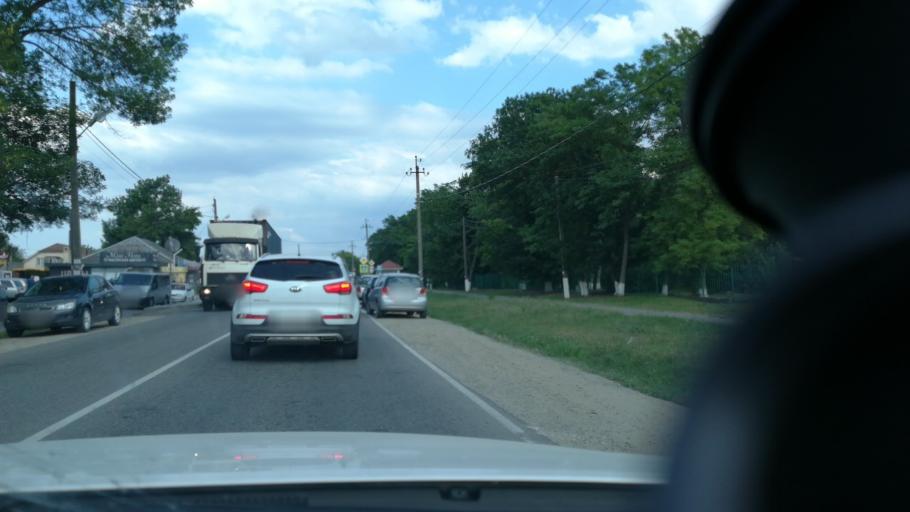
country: RU
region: Krasnodarskiy
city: Gostagayevskaya
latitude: 45.0257
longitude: 37.5004
